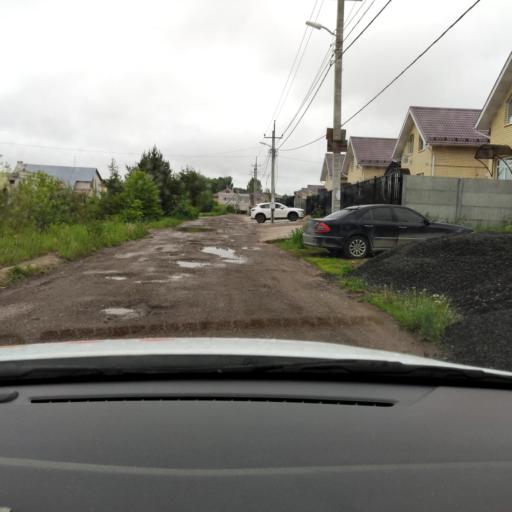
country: RU
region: Tatarstan
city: Stolbishchi
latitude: 55.7523
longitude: 49.2567
